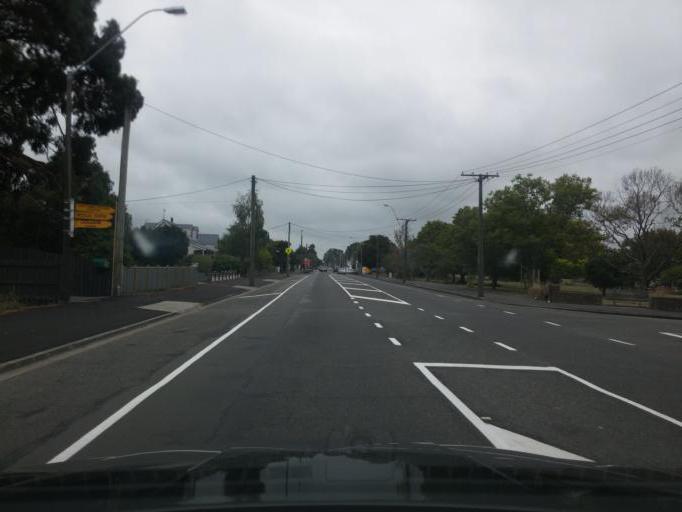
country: NZ
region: Wellington
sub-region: Masterton District
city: Masterton
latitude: -41.0894
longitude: 175.4504
